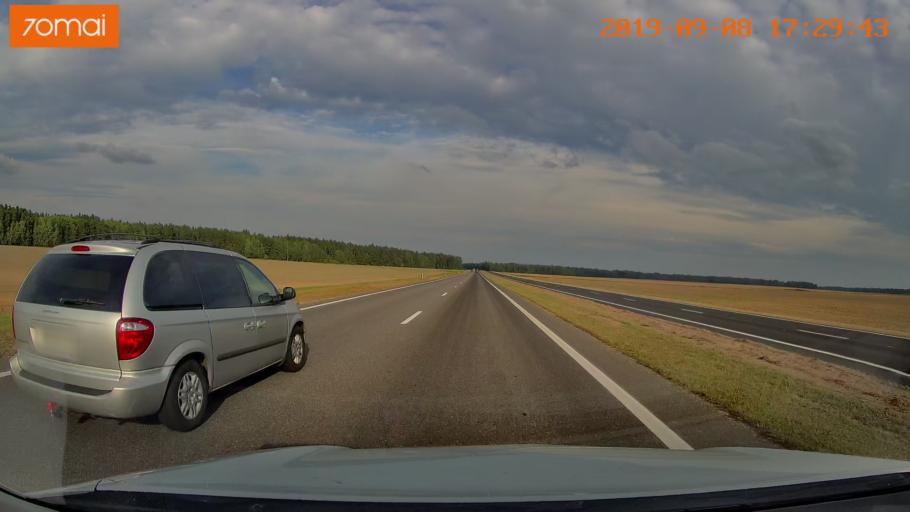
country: BY
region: Grodnenskaya
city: Skidal'
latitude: 53.5830
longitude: 24.4350
